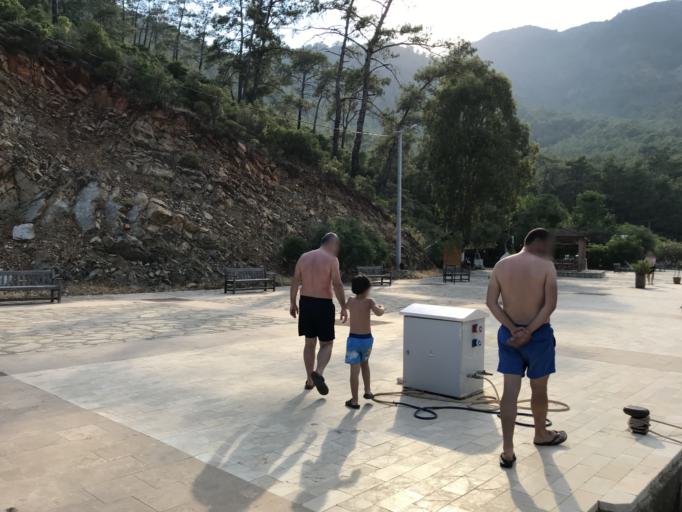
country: TR
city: Dalyan
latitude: 36.8278
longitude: 28.5496
